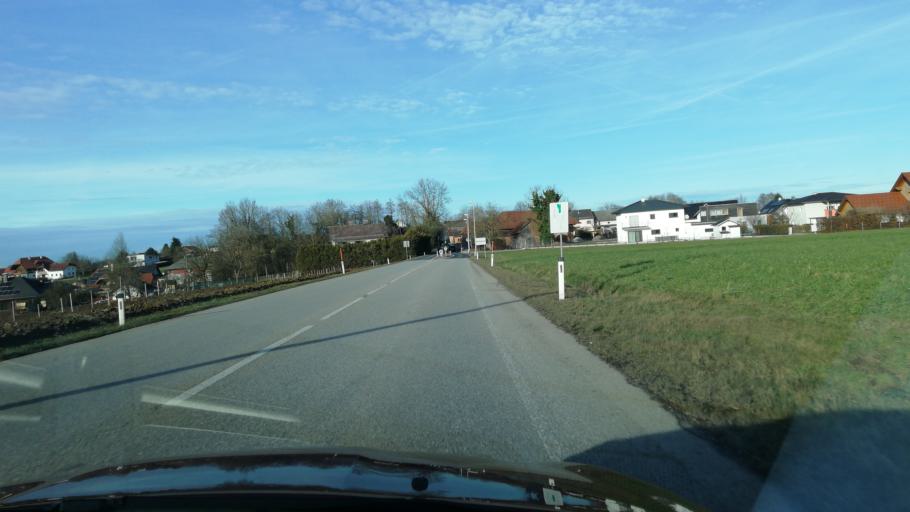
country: AT
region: Upper Austria
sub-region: Wels-Land
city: Sattledt
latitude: 48.0066
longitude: 14.0632
